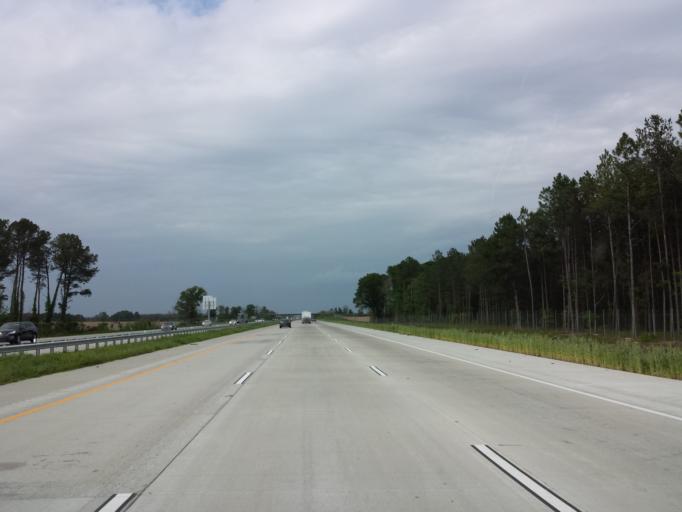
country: US
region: Georgia
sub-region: Dooly County
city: Vienna
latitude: 32.1372
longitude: -83.7583
